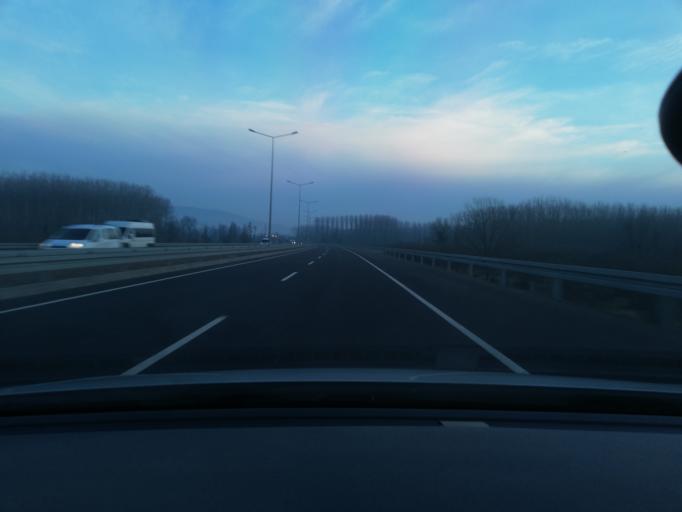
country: TR
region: Duzce
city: Duzce
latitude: 40.8098
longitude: 31.1691
